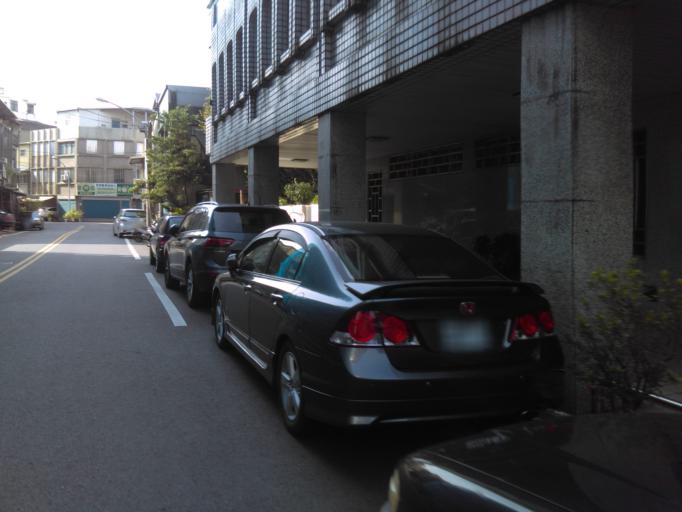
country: TW
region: Taiwan
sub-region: Yilan
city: Yilan
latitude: 24.7520
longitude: 121.7510
